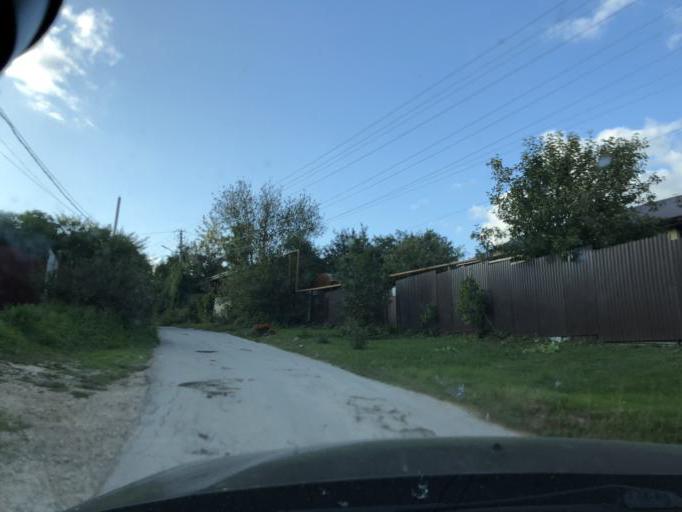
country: RU
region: Tula
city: Kosaya Gora
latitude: 54.1810
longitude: 37.5386
